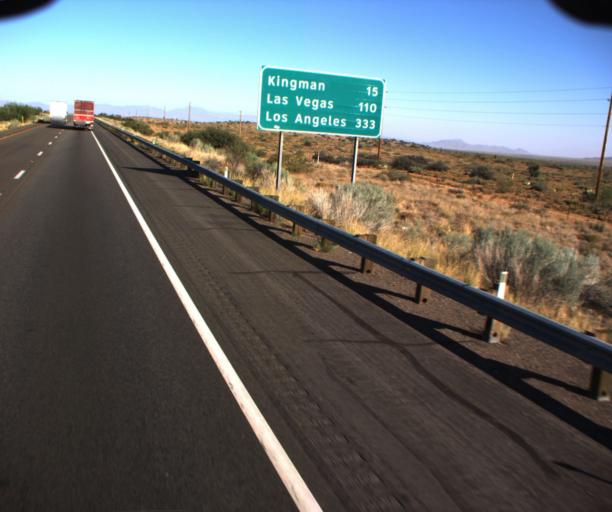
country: US
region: Arizona
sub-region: Mohave County
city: New Kingman-Butler
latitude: 35.1832
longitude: -113.8041
